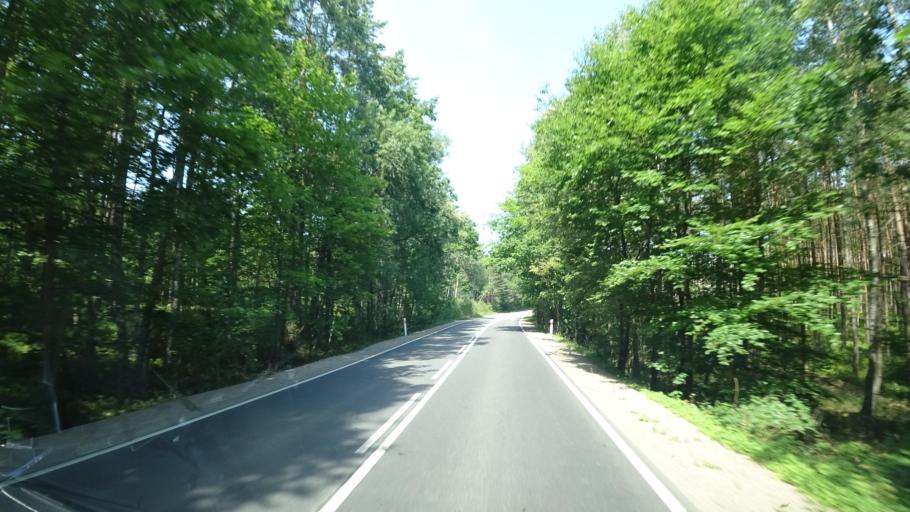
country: PL
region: Pomeranian Voivodeship
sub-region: Powiat koscierski
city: Dziemiany
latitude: 53.9873
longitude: 17.7703
